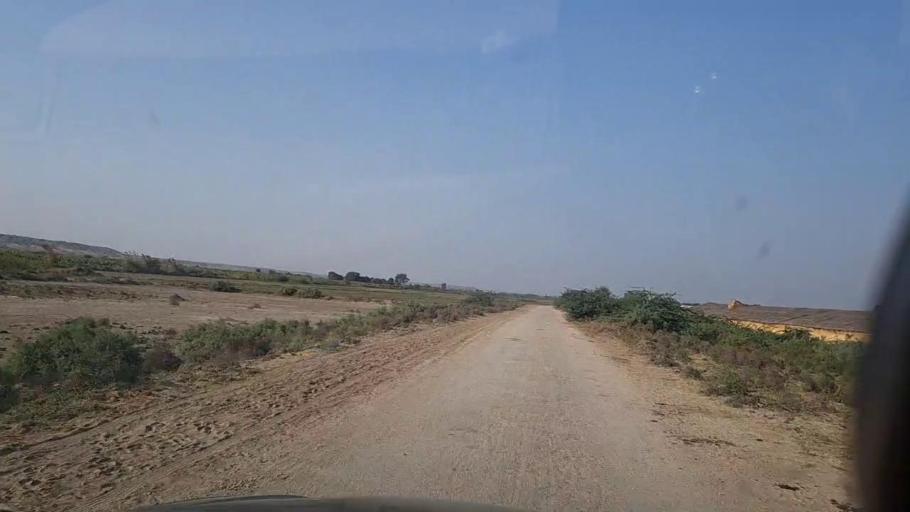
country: PK
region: Sindh
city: Thatta
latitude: 24.5989
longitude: 67.8742
